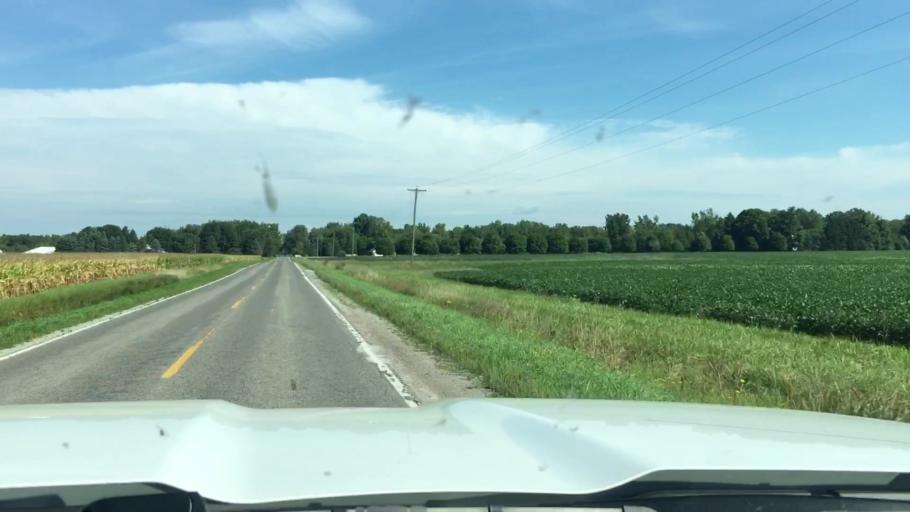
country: US
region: Michigan
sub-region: Saginaw County
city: Hemlock
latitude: 43.4665
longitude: -84.2303
